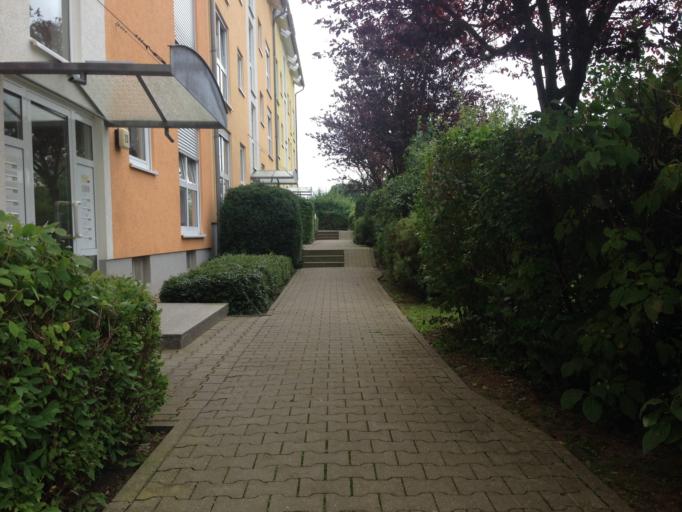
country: DE
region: Saxony
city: Wilkau-Hasslau
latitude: 50.6686
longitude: 12.5063
